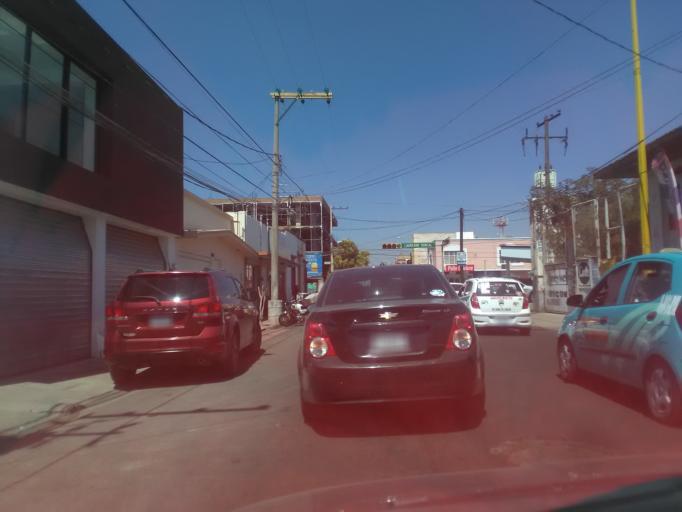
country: MX
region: Durango
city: Victoria de Durango
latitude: 24.0254
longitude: -104.6572
